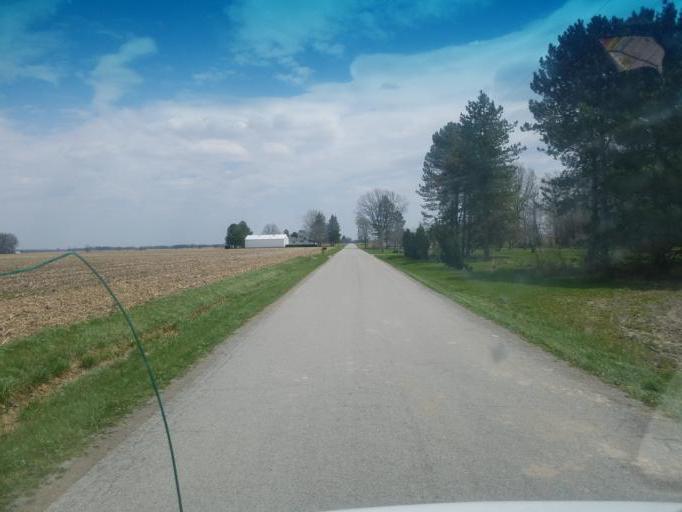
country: US
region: Ohio
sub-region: Wyandot County
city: Upper Sandusky
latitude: 40.7888
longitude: -83.3199
